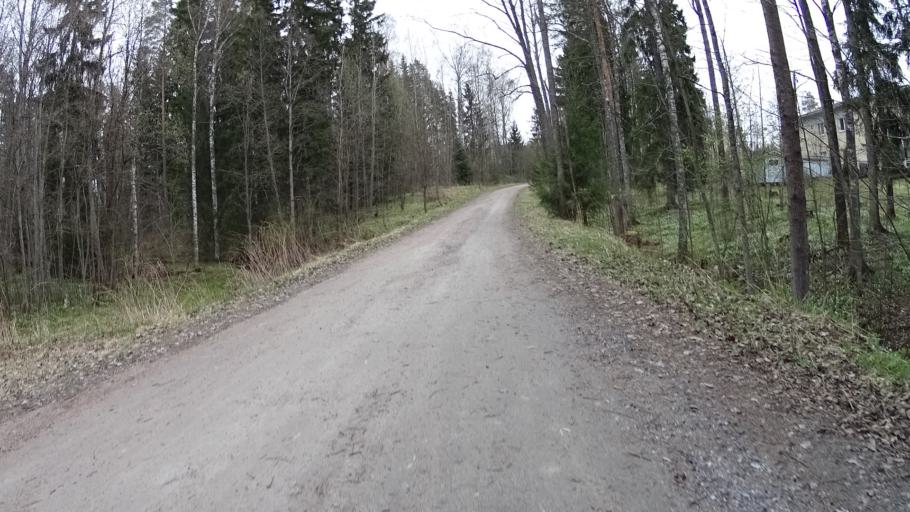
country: FI
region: Uusimaa
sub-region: Helsinki
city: Kilo
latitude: 60.2415
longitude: 24.7994
